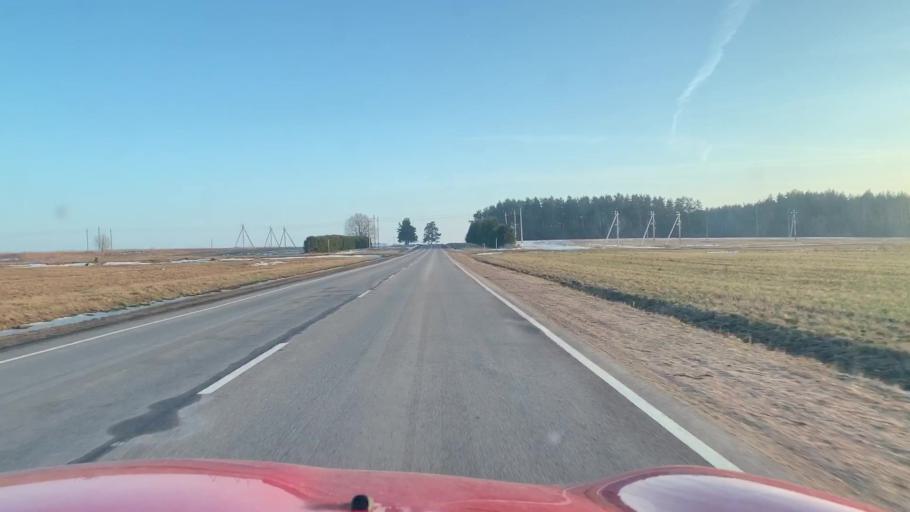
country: BY
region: Grodnenskaya
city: Mir
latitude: 53.4448
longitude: 26.4753
